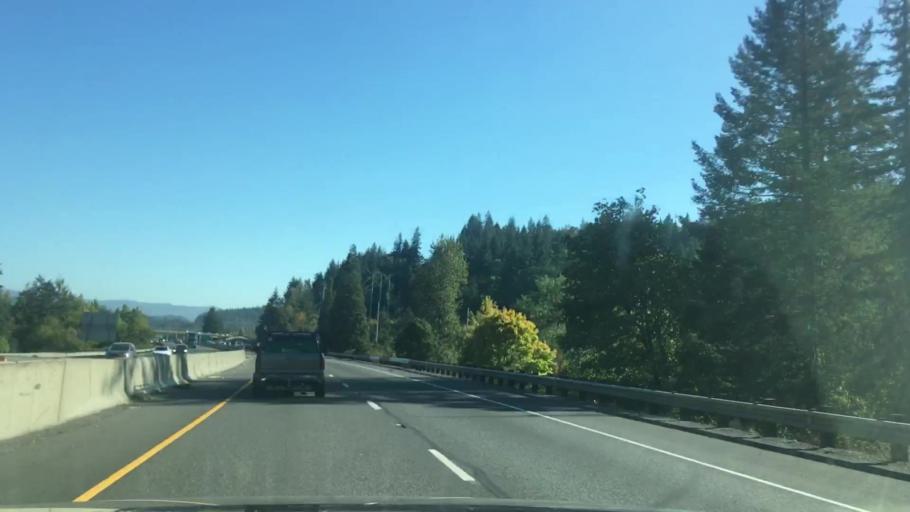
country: US
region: Oregon
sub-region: Lane County
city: Springfield
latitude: 44.0280
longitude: -123.0298
